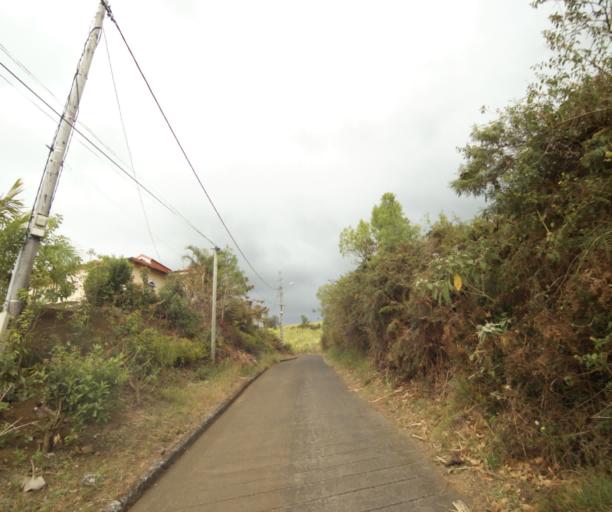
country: RE
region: Reunion
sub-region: Reunion
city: Saint-Paul
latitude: -21.0304
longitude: 55.3148
